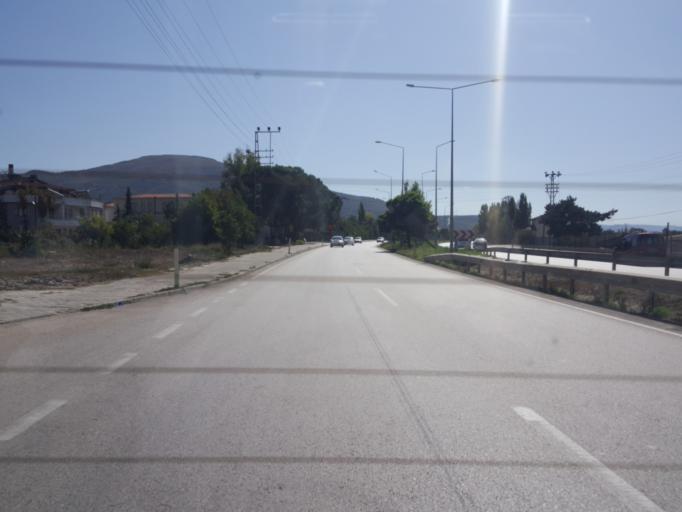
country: TR
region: Amasya
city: Amasya
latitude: 40.6052
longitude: 35.8122
